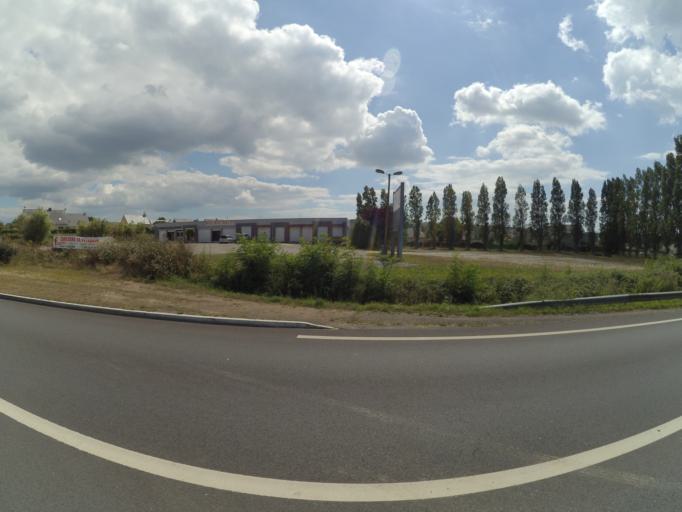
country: FR
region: Brittany
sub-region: Departement du Morbihan
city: Lanester
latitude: 47.7678
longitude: -3.3156
